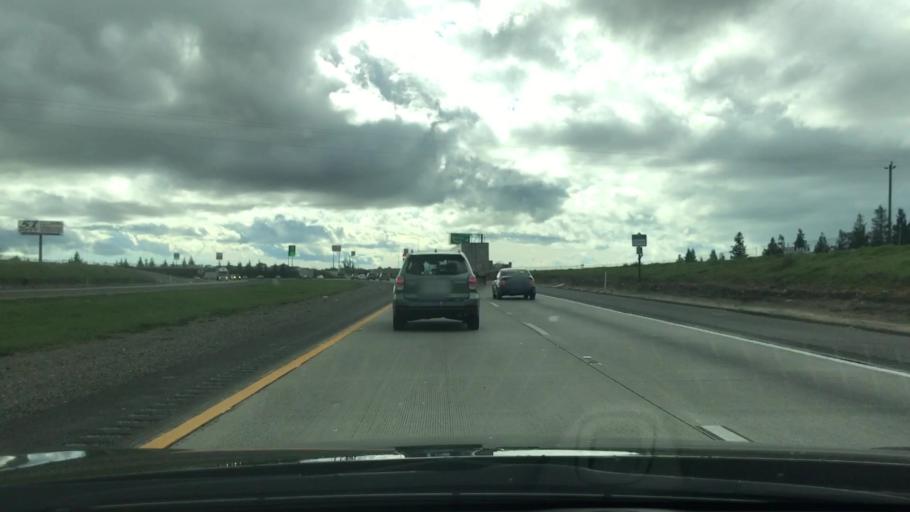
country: US
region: California
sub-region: Merced County
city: Livingston
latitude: 37.3949
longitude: -120.7406
